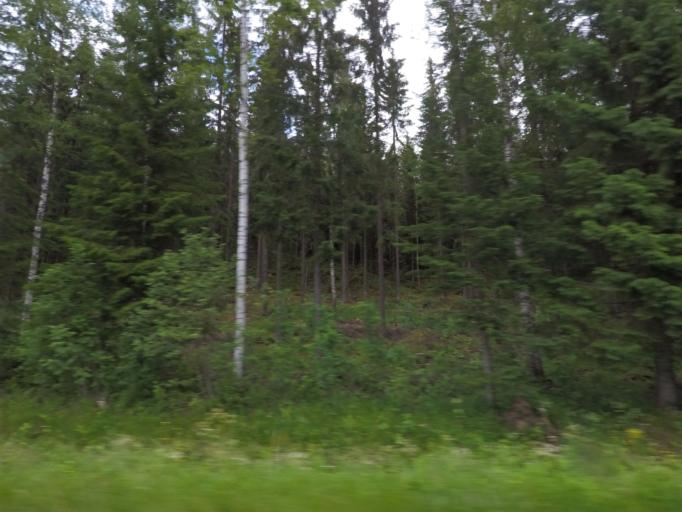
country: FI
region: Uusimaa
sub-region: Porvoo
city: Pukkila
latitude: 60.7925
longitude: 25.4667
